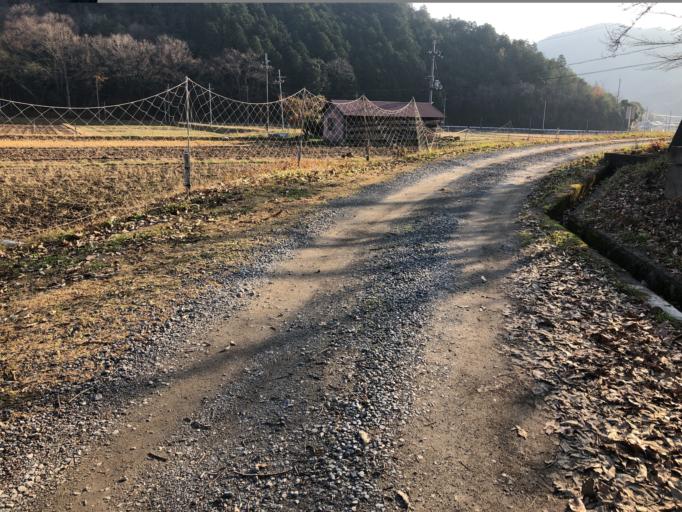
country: JP
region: Kyoto
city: Kameoka
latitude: 35.0564
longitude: 135.4760
